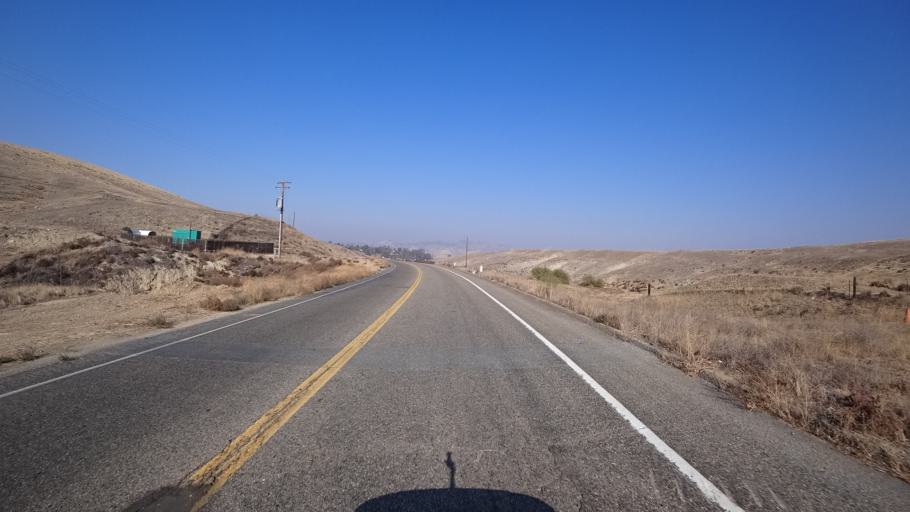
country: US
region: California
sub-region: Kern County
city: Oildale
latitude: 35.4222
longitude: -118.8578
